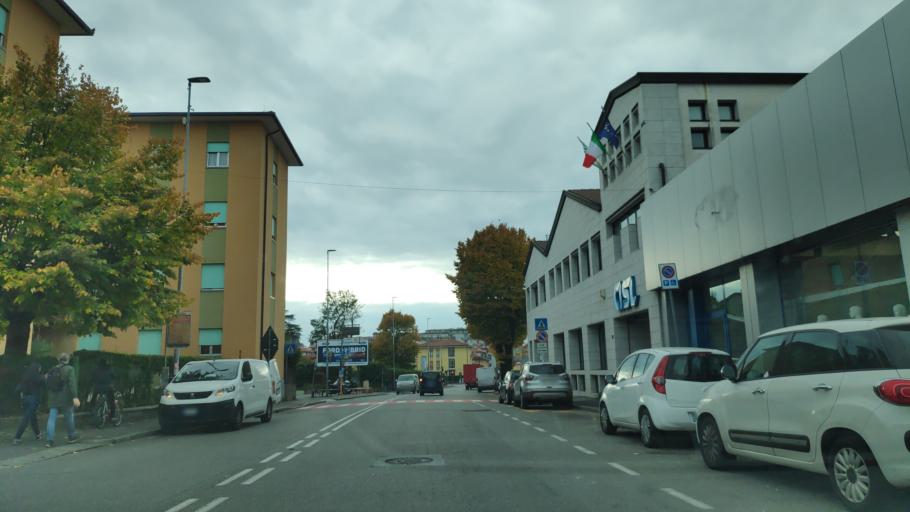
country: IT
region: Lombardy
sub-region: Provincia di Bergamo
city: Bergamo
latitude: 45.6869
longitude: 9.6703
